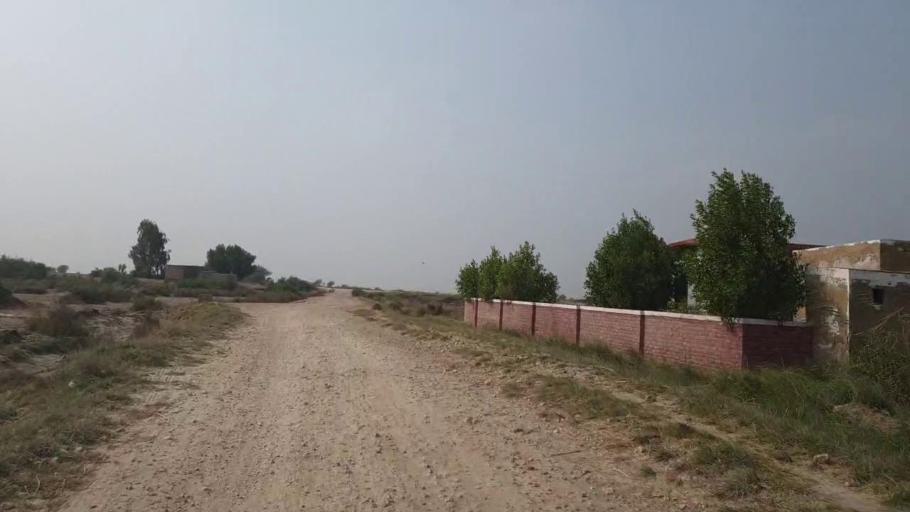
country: PK
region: Sindh
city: Kario
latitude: 24.8775
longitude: 68.5043
